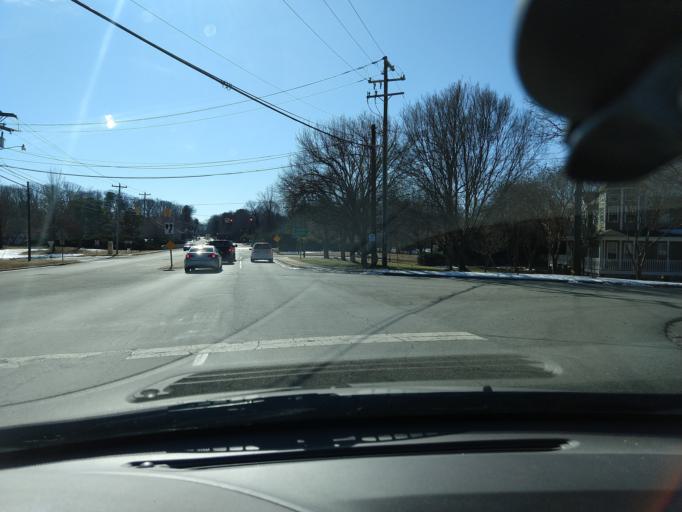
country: US
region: North Carolina
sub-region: Guilford County
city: Greensboro
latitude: 36.1145
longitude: -79.8506
